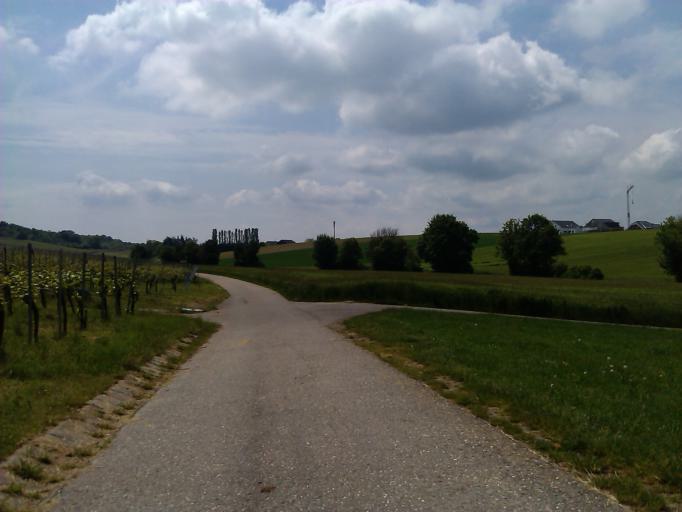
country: DE
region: Baden-Wuerttemberg
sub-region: Regierungsbezirk Stuttgart
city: Pfaffenhofen
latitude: 49.0995
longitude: 8.9839
